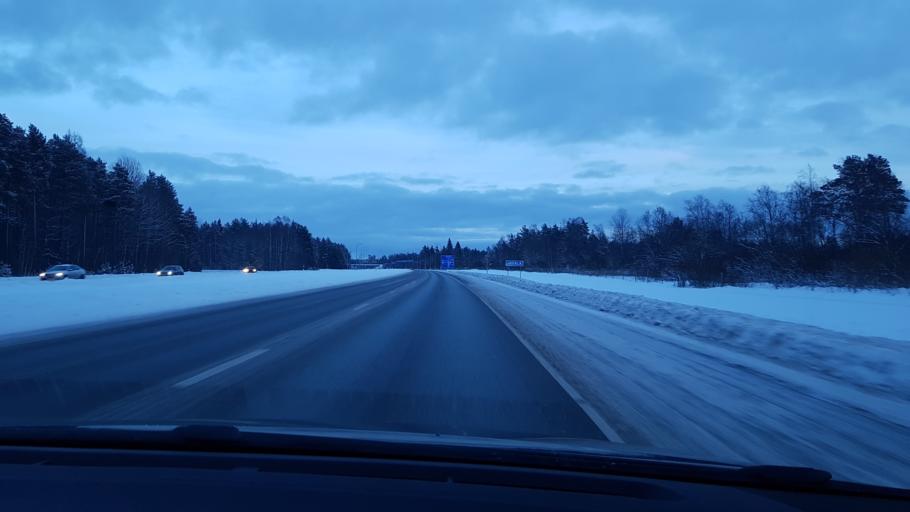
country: EE
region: Harju
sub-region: Raasiku vald
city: Raasiku
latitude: 59.4349
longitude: 25.1718
